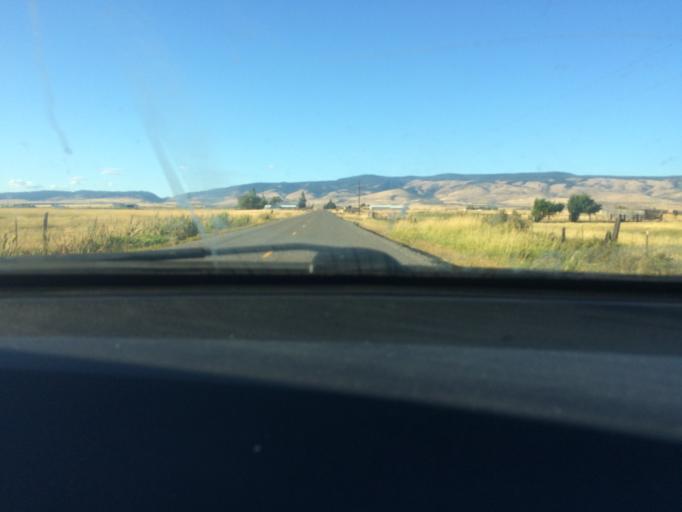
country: US
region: Washington
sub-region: Kittitas County
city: Ellensburg
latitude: 47.0834
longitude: -120.6033
